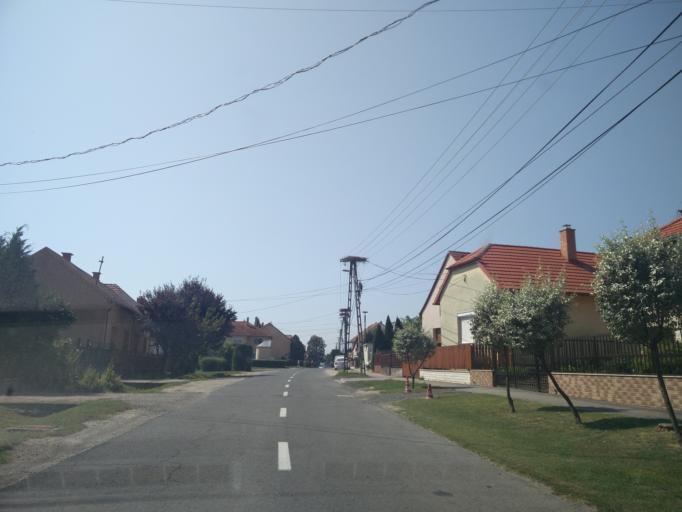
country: HU
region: Zala
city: Zalaegerszeg
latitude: 46.8504
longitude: 16.8804
